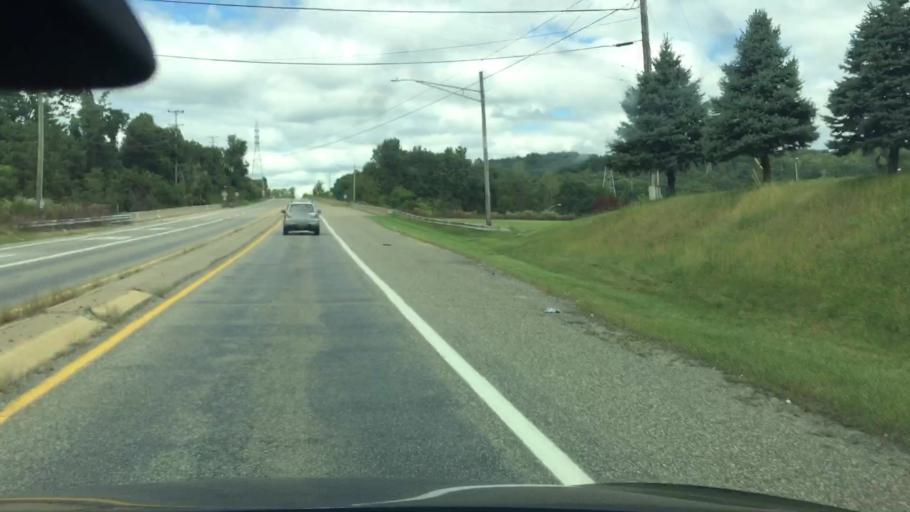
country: US
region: Pennsylvania
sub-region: Allegheny County
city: Cheswick
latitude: 40.5486
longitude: -79.8193
